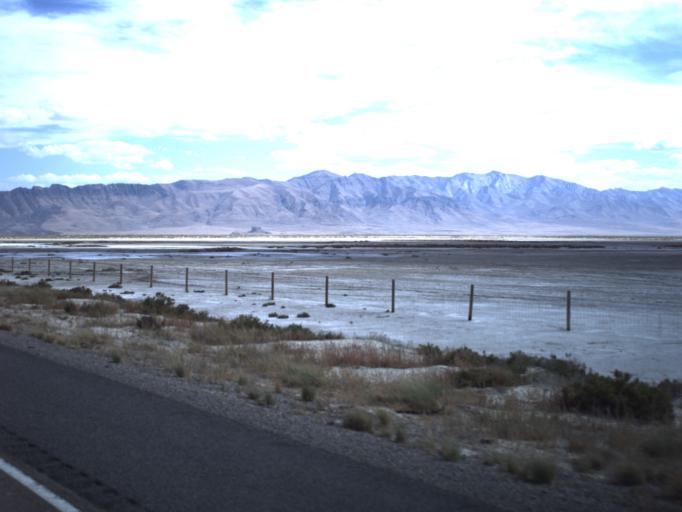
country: US
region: Utah
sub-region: Tooele County
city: Grantsville
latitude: 40.7563
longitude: -112.7598
